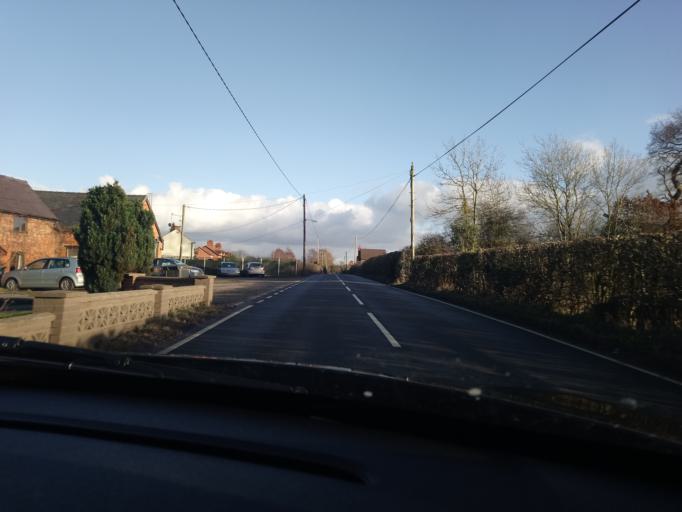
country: GB
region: Wales
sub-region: Wrexham
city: Overton
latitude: 52.9226
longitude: -2.9320
